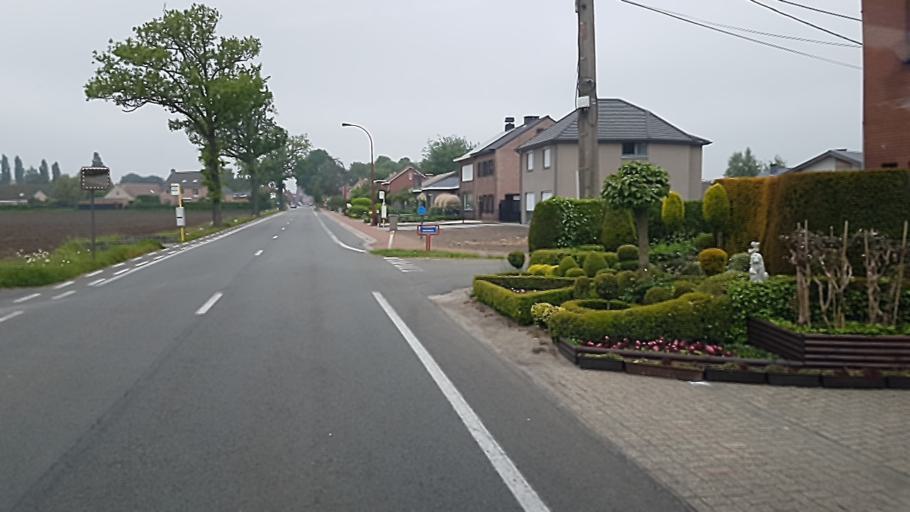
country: BE
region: Flanders
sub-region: Provincie Antwerpen
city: Kalmthout
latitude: 51.3964
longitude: 4.5111
